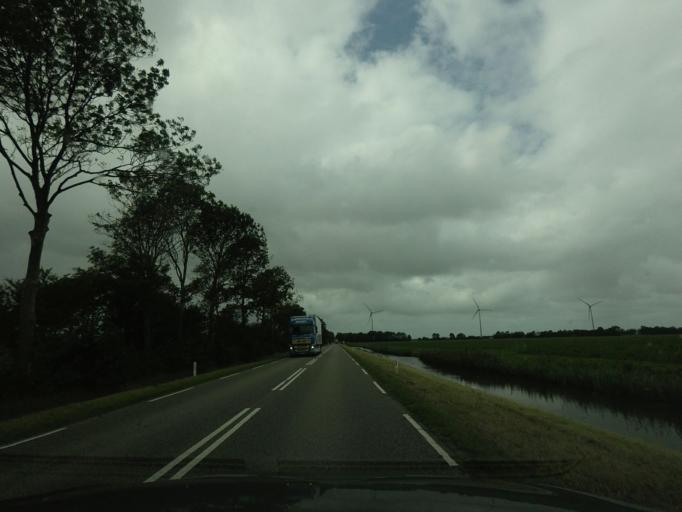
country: NL
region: North Holland
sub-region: Gemeente Schagen
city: Harenkarspel
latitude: 52.7184
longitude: 4.7835
